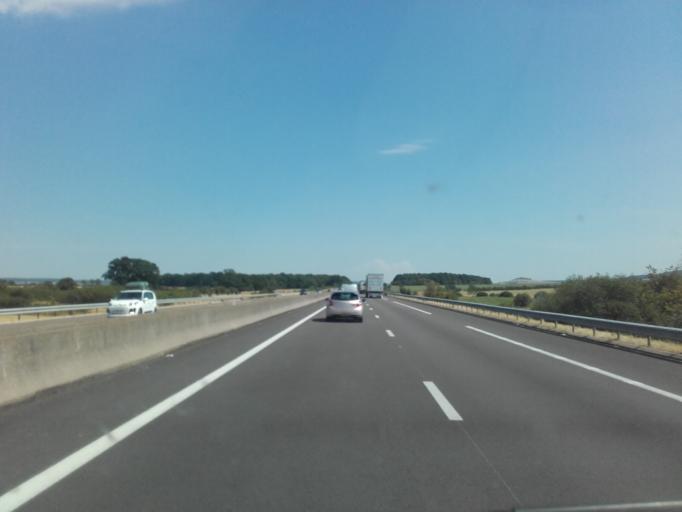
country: FR
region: Bourgogne
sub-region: Departement de la Cote-d'Or
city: Semur-en-Auxois
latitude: 47.3706
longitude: 4.4005
